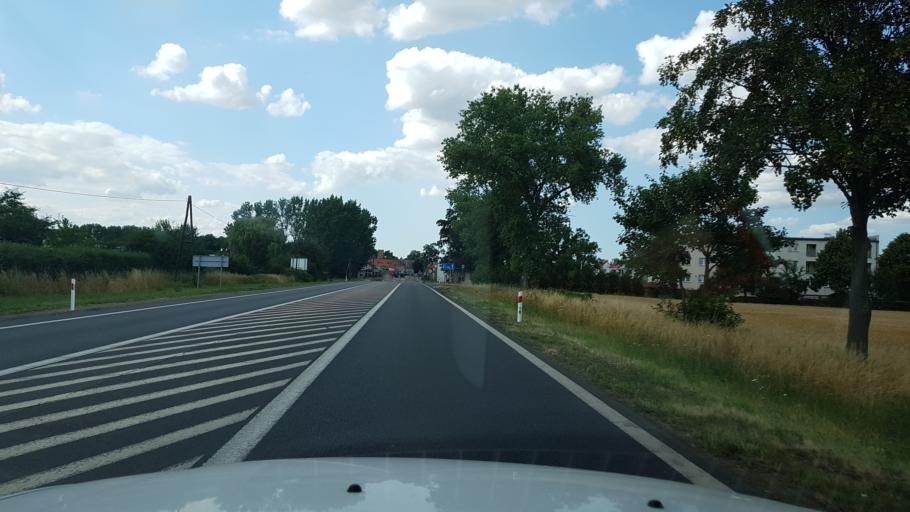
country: PL
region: West Pomeranian Voivodeship
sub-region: Powiat pyrzycki
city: Pyrzyce
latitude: 53.1810
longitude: 14.8435
